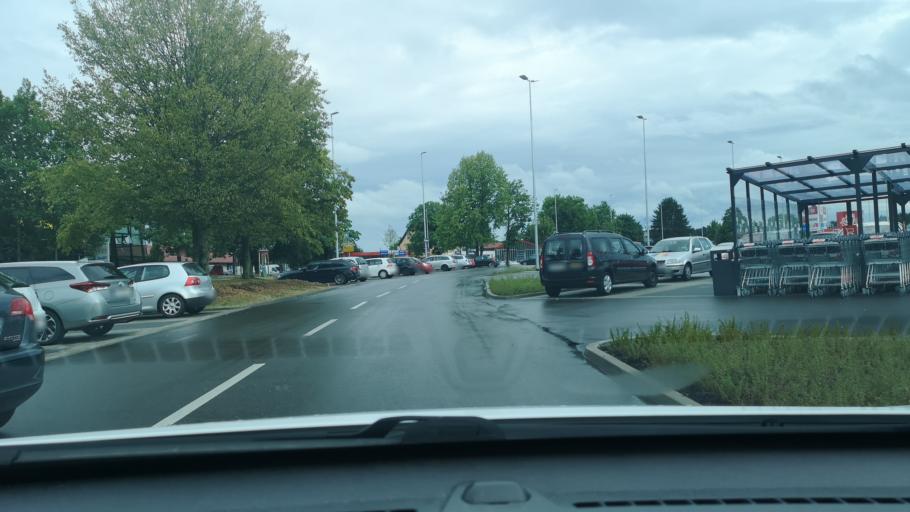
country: DE
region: Baden-Wuerttemberg
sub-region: Freiburg Region
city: Rottweil
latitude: 48.1498
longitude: 8.6405
